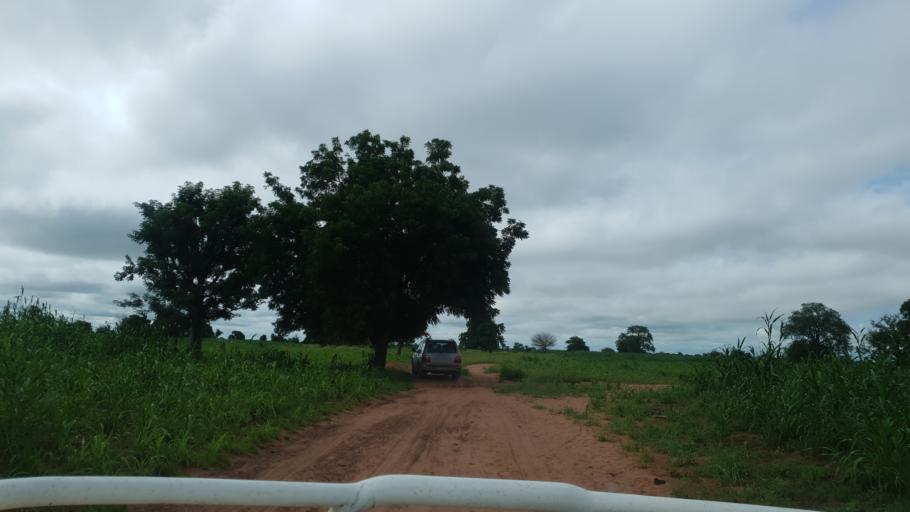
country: ML
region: Segou
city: Baroueli
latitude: 13.5007
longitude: -6.8977
